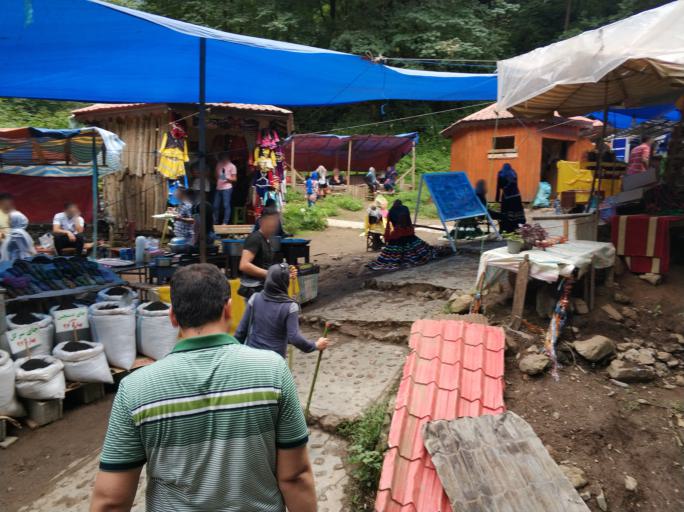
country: IR
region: Gilan
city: Fuman
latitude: 37.0683
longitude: 49.2459
